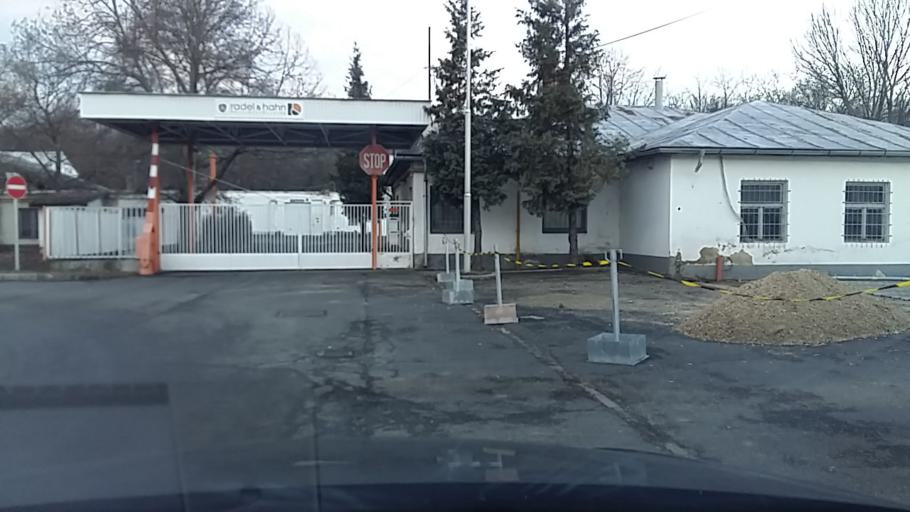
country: HU
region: Hajdu-Bihar
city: Debrecen
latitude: 47.5514
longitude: 21.6477
